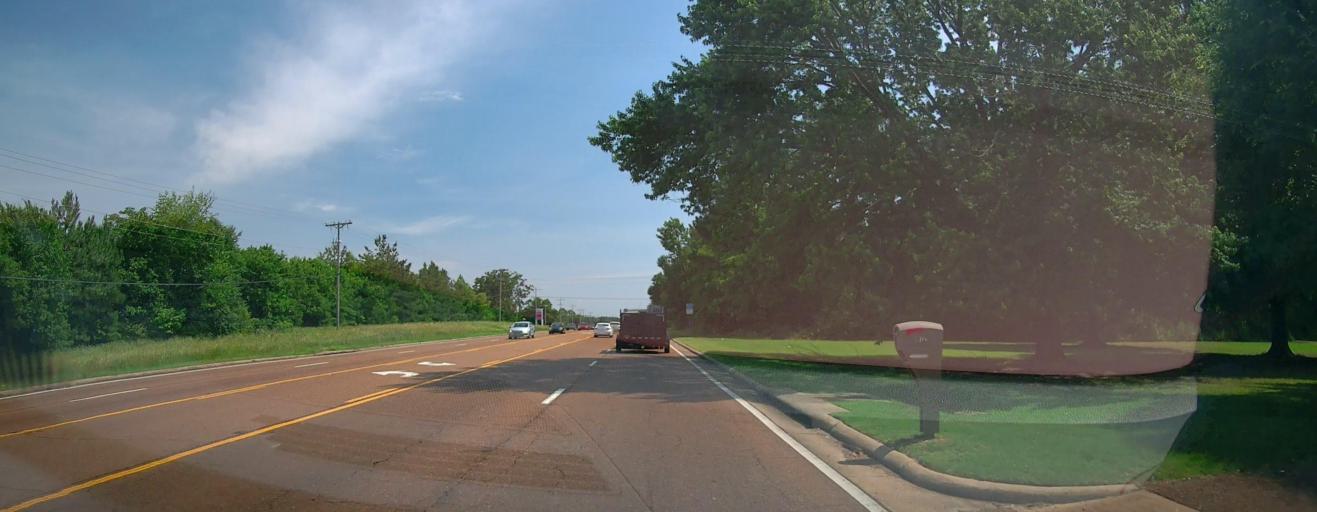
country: US
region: Mississippi
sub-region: De Soto County
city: Olive Branch
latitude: 34.9938
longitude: -89.8308
